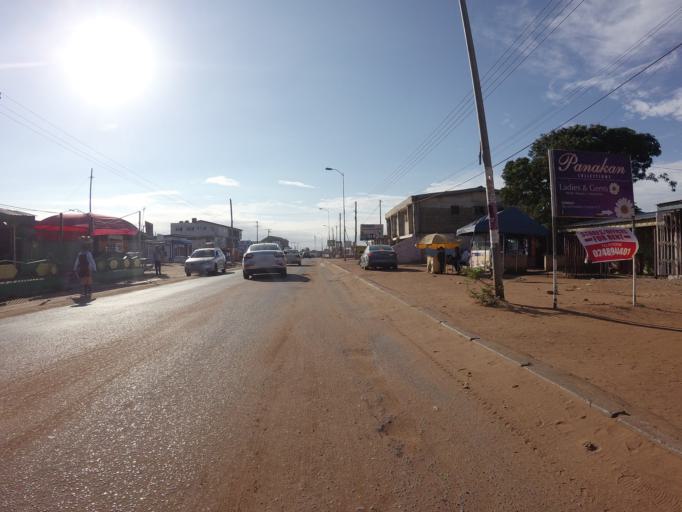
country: GH
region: Greater Accra
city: Tema
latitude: 5.6466
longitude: -0.0593
